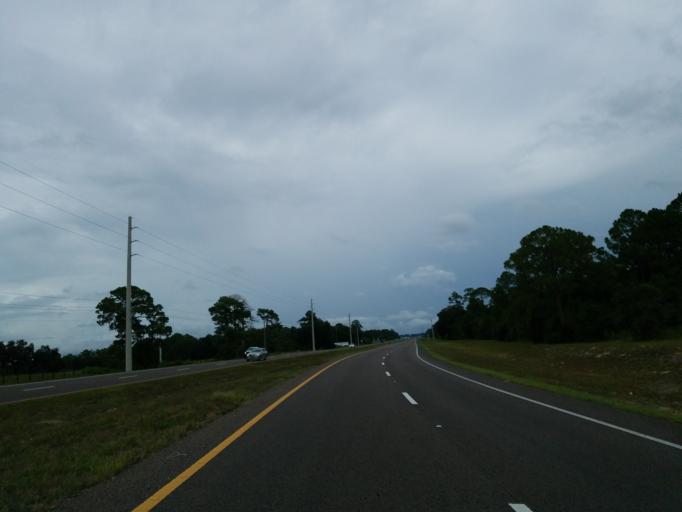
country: US
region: Florida
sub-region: Sumter County
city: Wildwood
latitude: 28.8801
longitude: -82.1237
